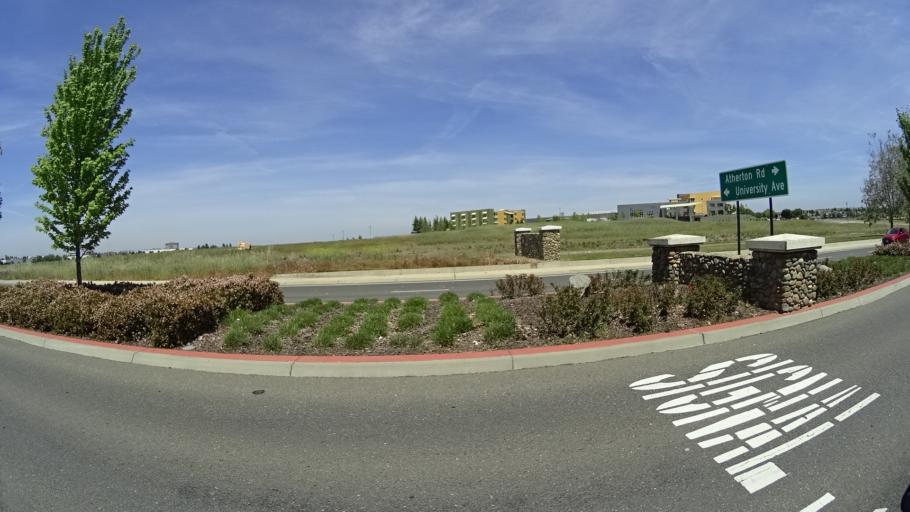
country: US
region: California
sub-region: Placer County
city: Rocklin
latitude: 38.8169
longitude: -121.2949
